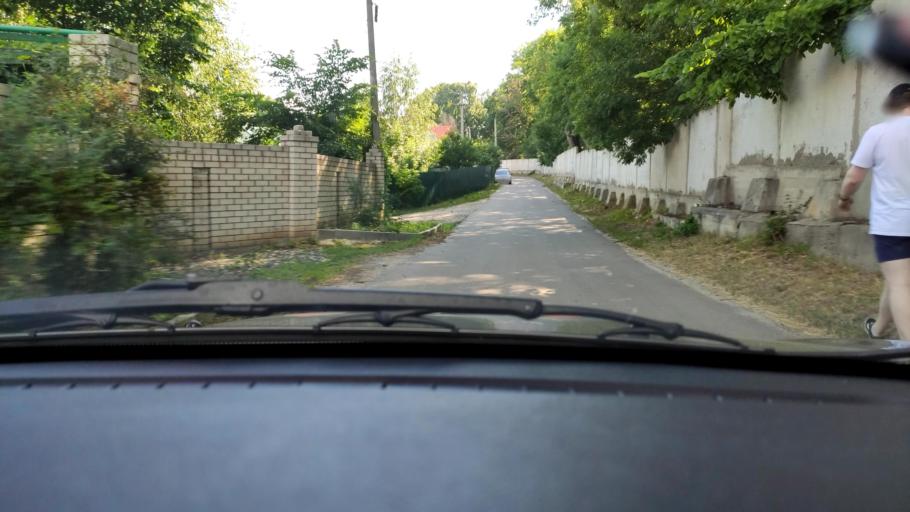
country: RU
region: Voronezj
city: Ramon'
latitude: 51.8232
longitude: 39.2692
